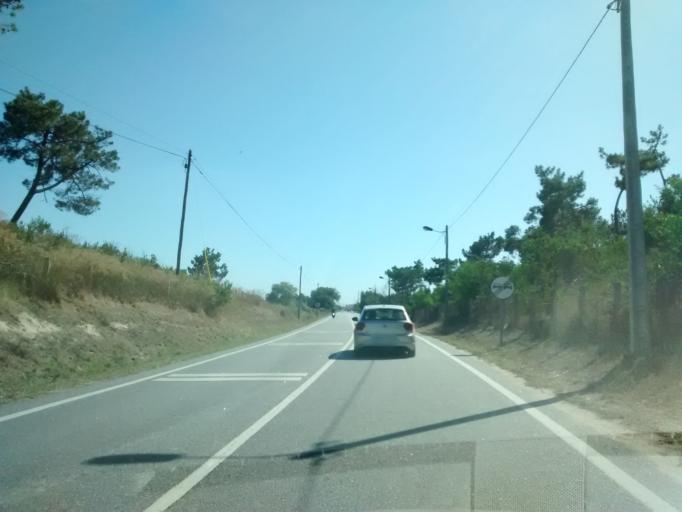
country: PT
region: Aveiro
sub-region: Ilhavo
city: Gafanha da Nazare
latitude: 40.6704
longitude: -8.7252
